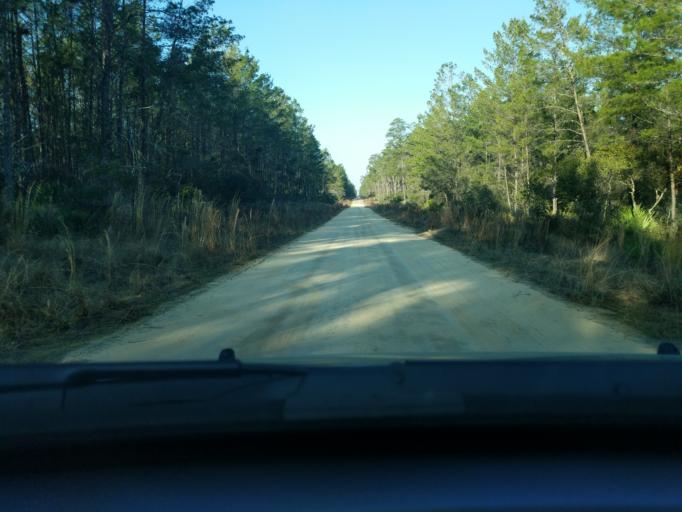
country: US
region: Florida
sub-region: Lake County
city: Astor
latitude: 29.2262
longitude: -81.7826
